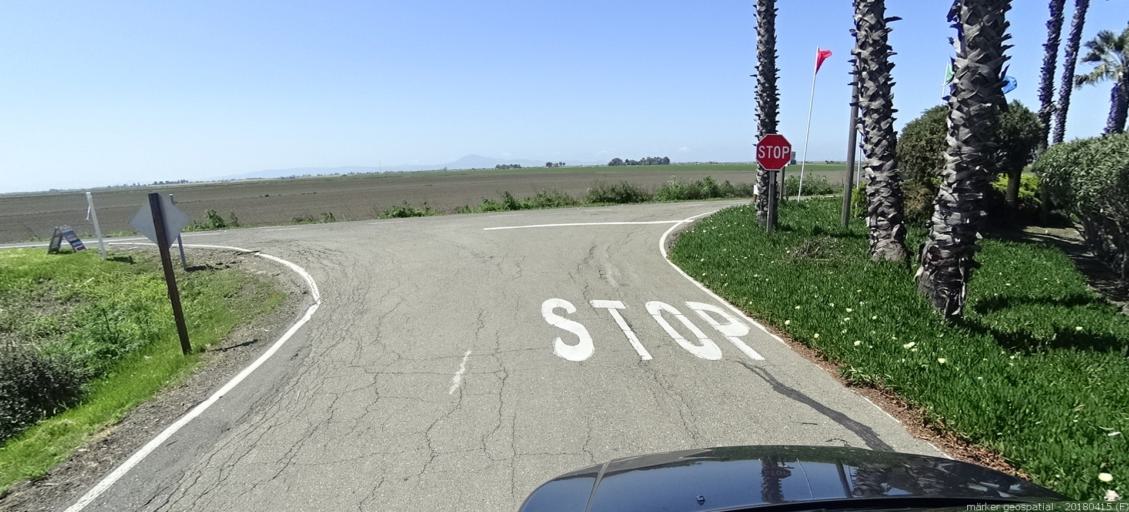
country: US
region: California
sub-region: Solano County
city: Rio Vista
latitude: 38.1473
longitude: -121.6049
